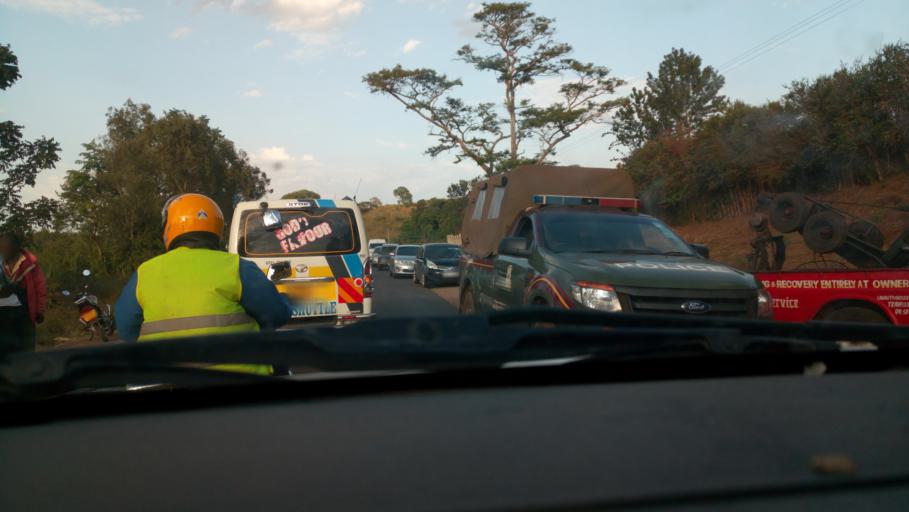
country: KE
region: Murang'a District
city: Maragua
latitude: -0.7774
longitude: 37.1456
